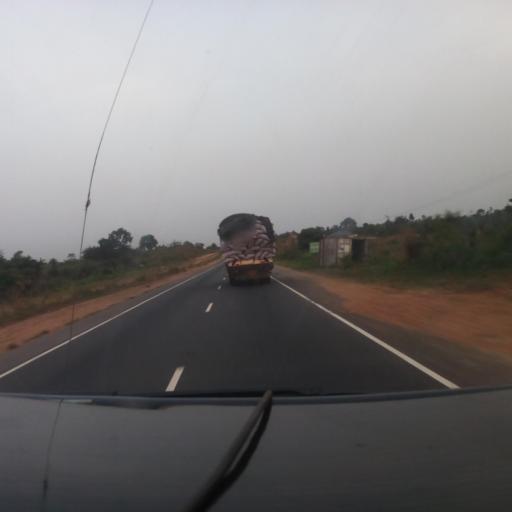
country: GH
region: Eastern
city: Nsawam
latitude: 5.8859
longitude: -0.3782
